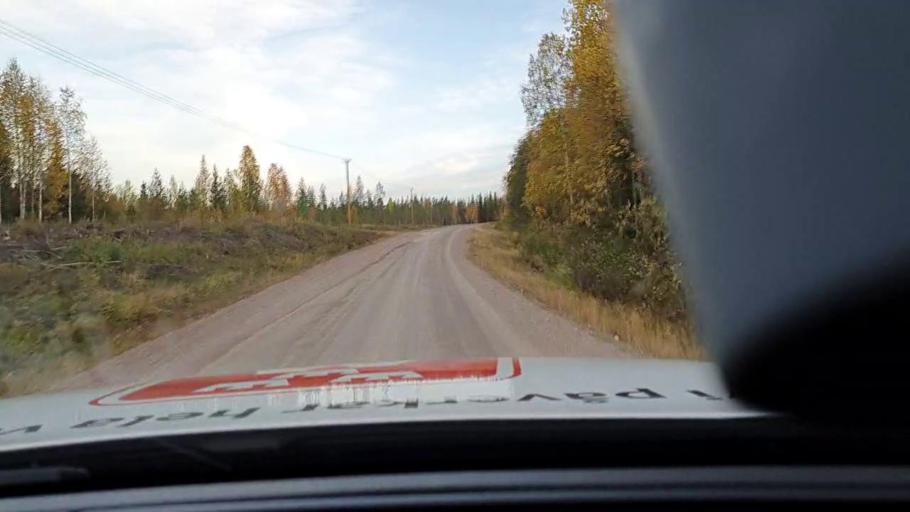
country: SE
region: Norrbotten
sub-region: Overkalix Kommun
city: OEverkalix
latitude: 66.3225
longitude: 22.6322
